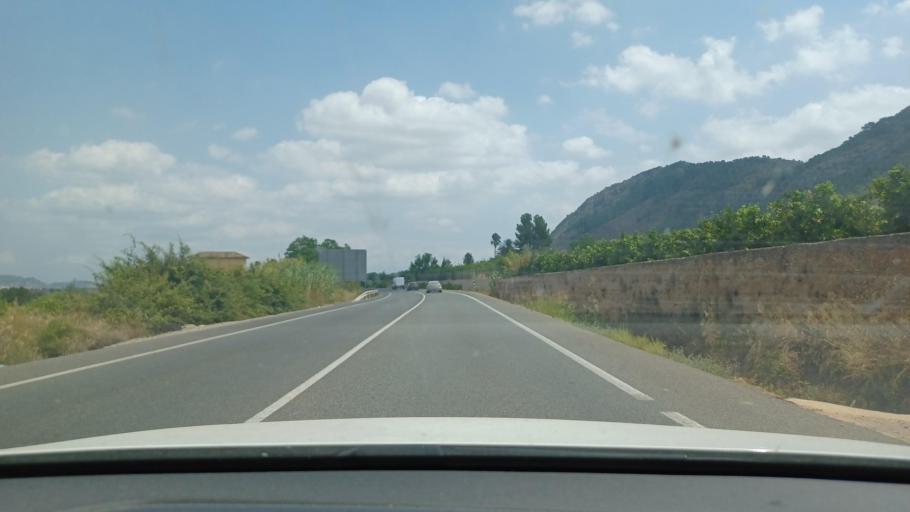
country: ES
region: Valencia
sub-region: Provincia de Valencia
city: Cerda
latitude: 38.9719
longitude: -0.5602
